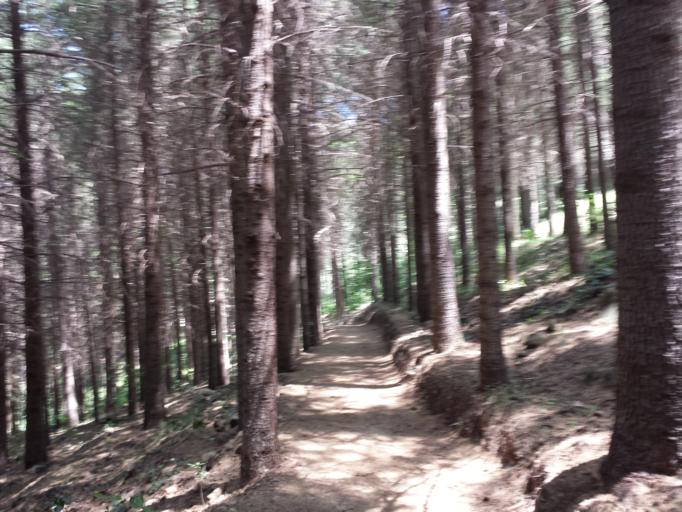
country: IT
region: Sicily
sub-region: Palermo
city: Petralia Sottana
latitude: 37.8411
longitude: 14.0964
